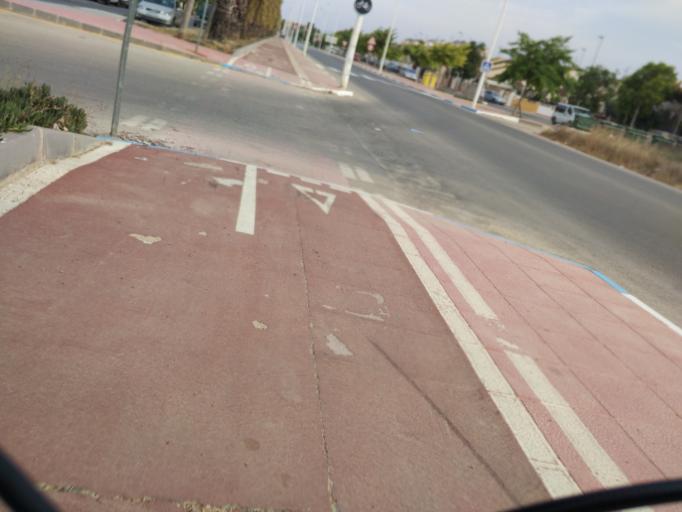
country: ES
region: Murcia
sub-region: Murcia
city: Los Alcazares
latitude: 37.7493
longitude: -0.8552
